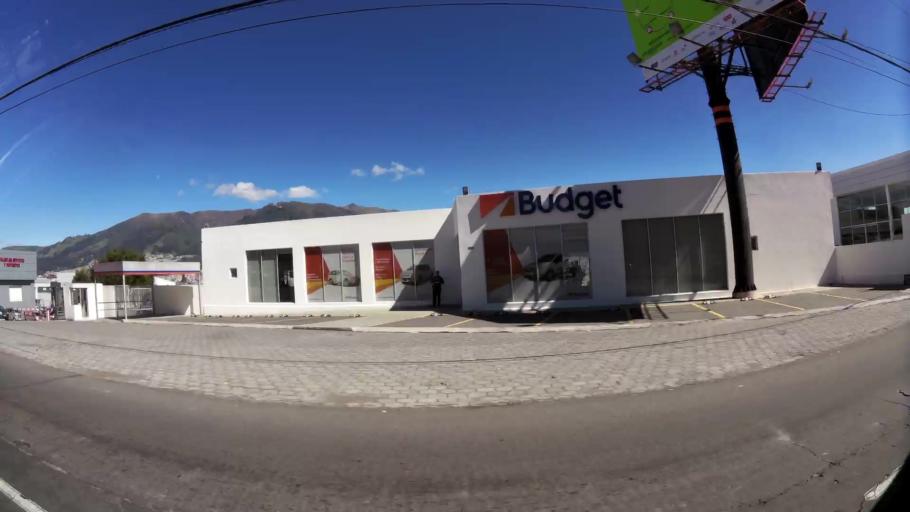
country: EC
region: Pichincha
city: Quito
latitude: -0.1691
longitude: -78.4697
